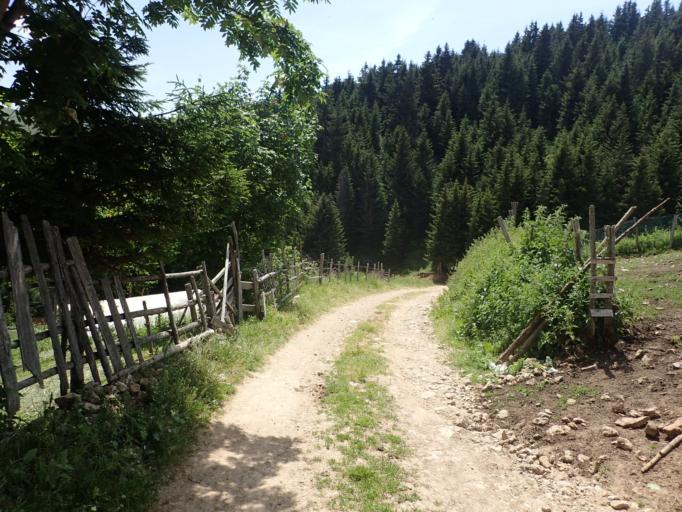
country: TR
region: Ordu
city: Topcam
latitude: 40.6419
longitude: 37.9538
